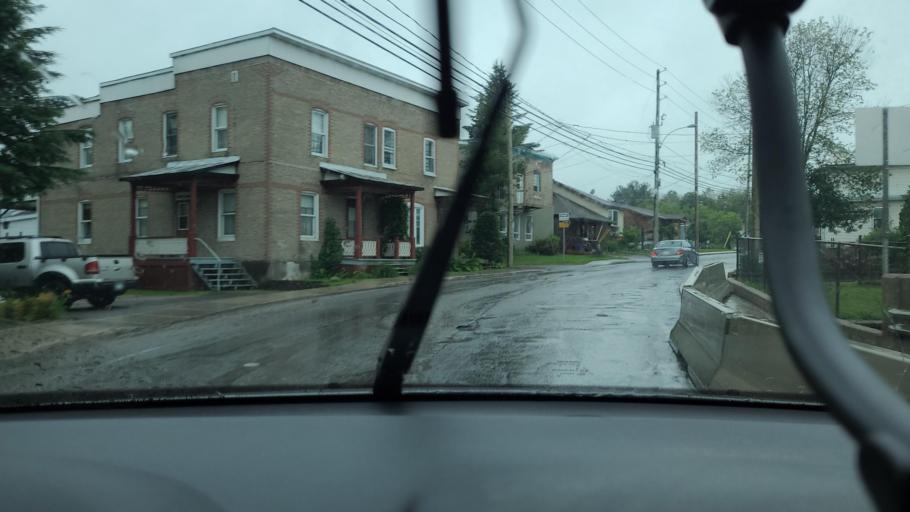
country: CA
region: Quebec
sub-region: Outaouais
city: Saint-Andre-Avellin
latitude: 45.7220
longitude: -75.0558
